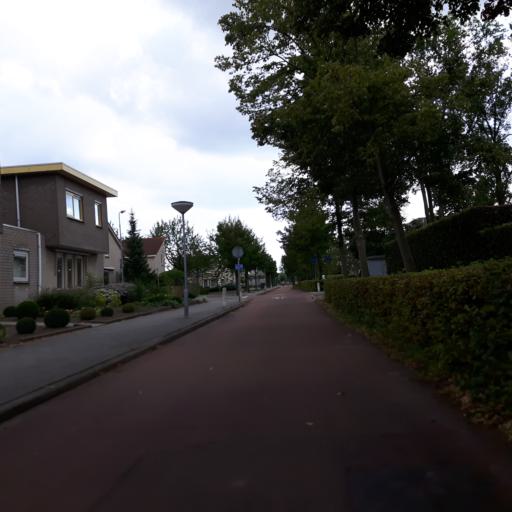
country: NL
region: Zeeland
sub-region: Gemeente Goes
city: Goes
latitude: 51.4896
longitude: 3.8995
